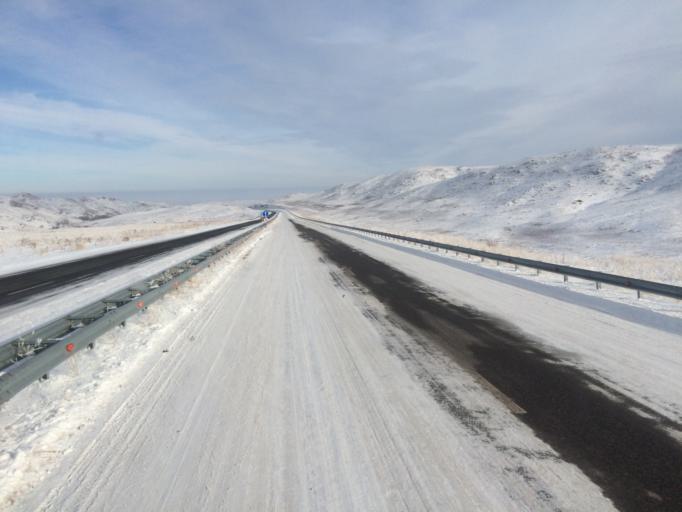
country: KZ
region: Zhambyl
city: Georgiyevka
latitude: 43.4280
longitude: 74.8937
